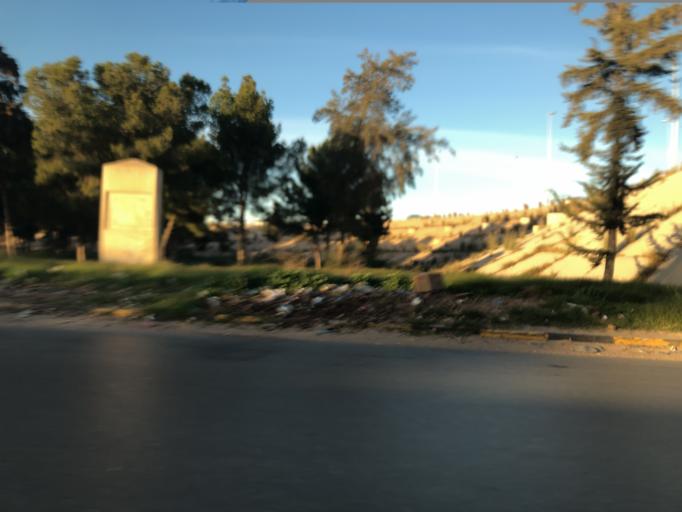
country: LY
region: Tripoli
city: Tagiura
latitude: 32.8689
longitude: 13.2891
